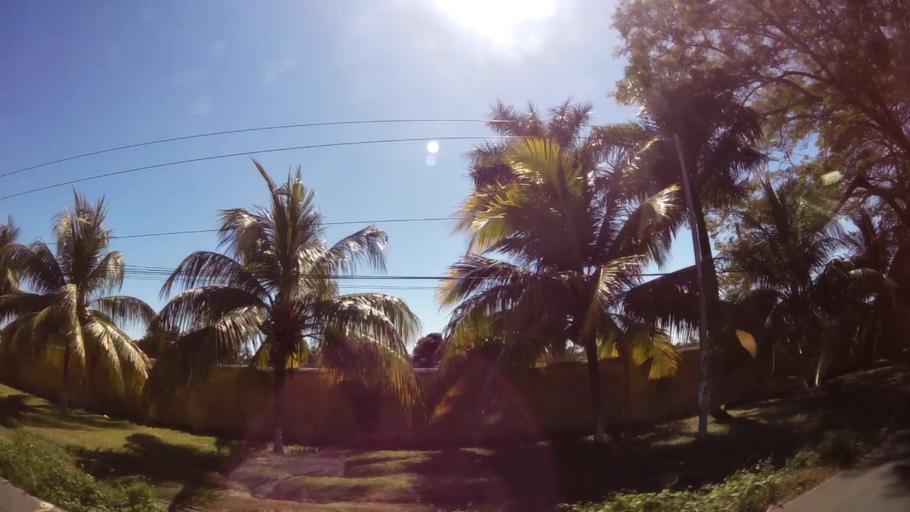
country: GT
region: Escuintla
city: Iztapa
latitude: 13.9390
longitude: -90.7216
